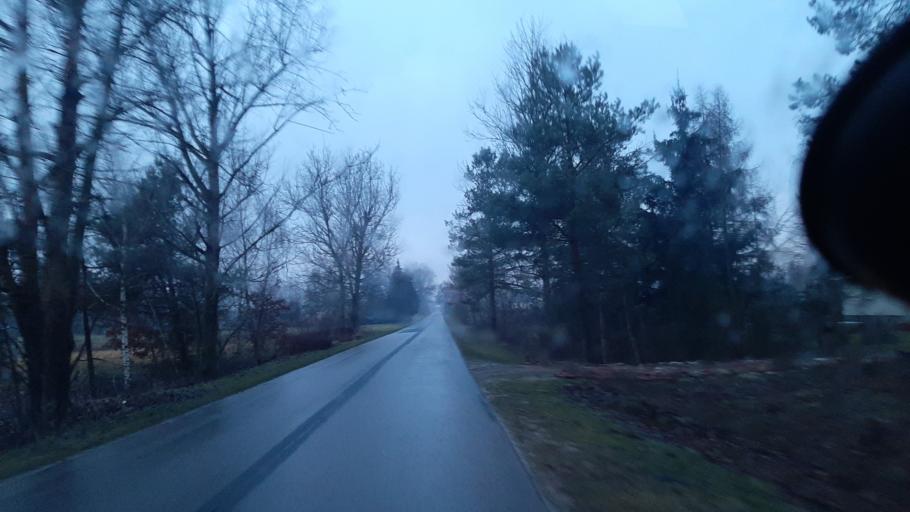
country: PL
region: Lublin Voivodeship
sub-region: Powiat lubartowski
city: Ostrowek
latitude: 51.5382
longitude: 22.5719
